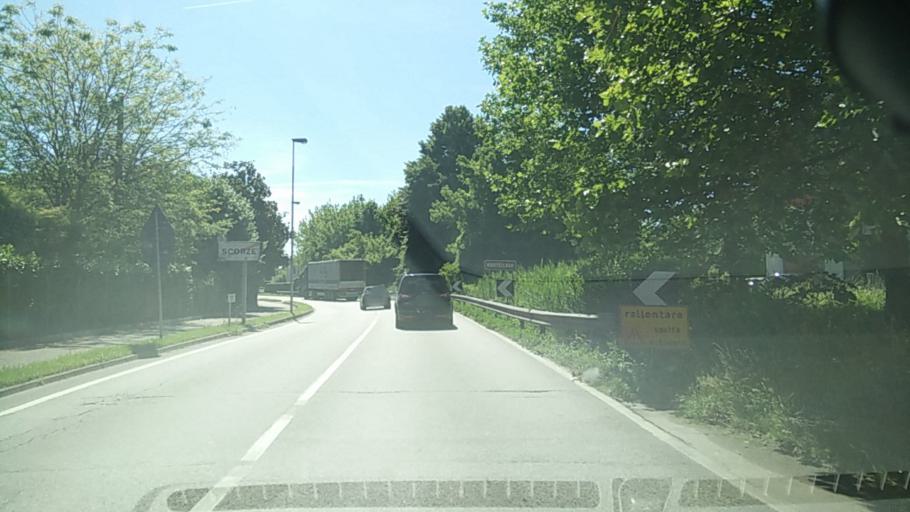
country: IT
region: Veneto
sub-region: Provincia di Venezia
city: Scorze
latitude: 45.5630
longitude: 12.1260
